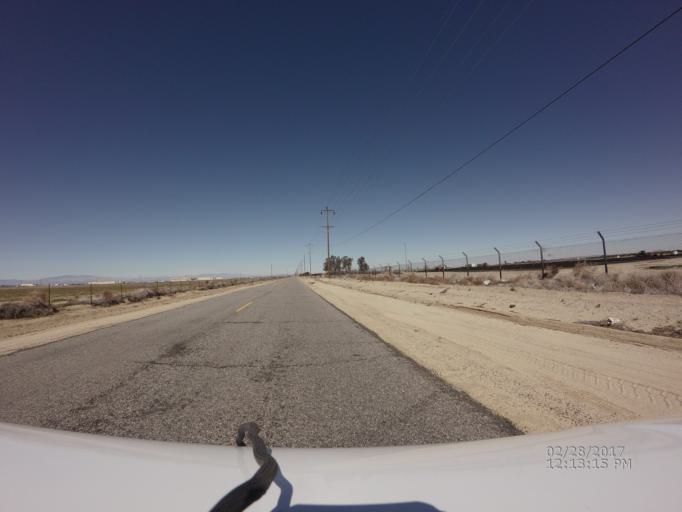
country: US
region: California
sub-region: Los Angeles County
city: Palmdale
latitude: 34.6130
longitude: -118.0586
